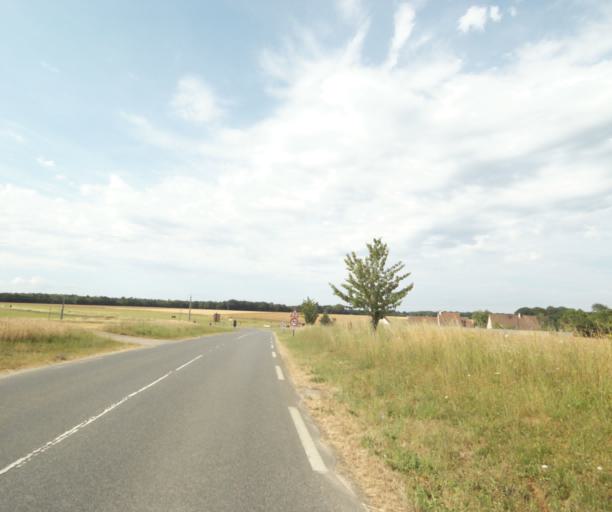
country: FR
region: Ile-de-France
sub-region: Departement de Seine-et-Marne
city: Acheres-la-Foret
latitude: 48.3419
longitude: 2.5952
